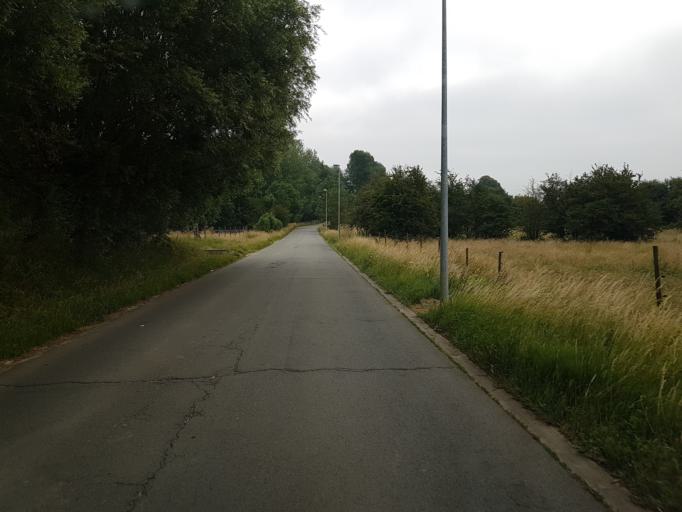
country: BE
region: Flanders
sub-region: Provincie Oost-Vlaanderen
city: Haaltert
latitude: 50.8757
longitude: 3.9814
